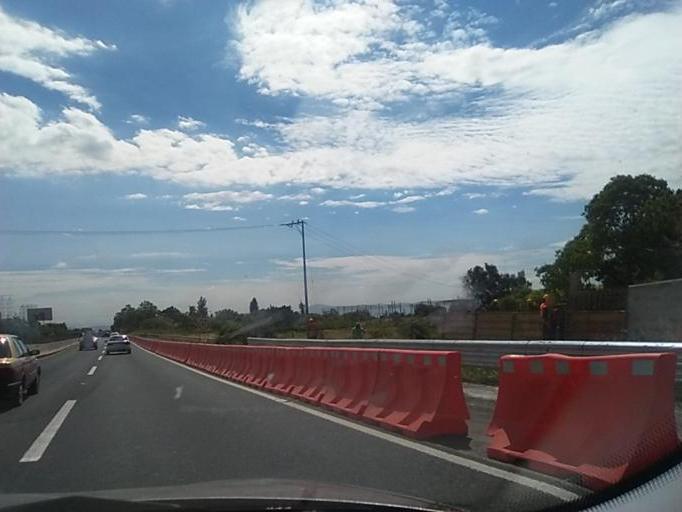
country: MX
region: Morelos
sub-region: Cuernavaca
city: Fraccionamiento Lomas de Ahuatlan
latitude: 18.9610
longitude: -99.2300
